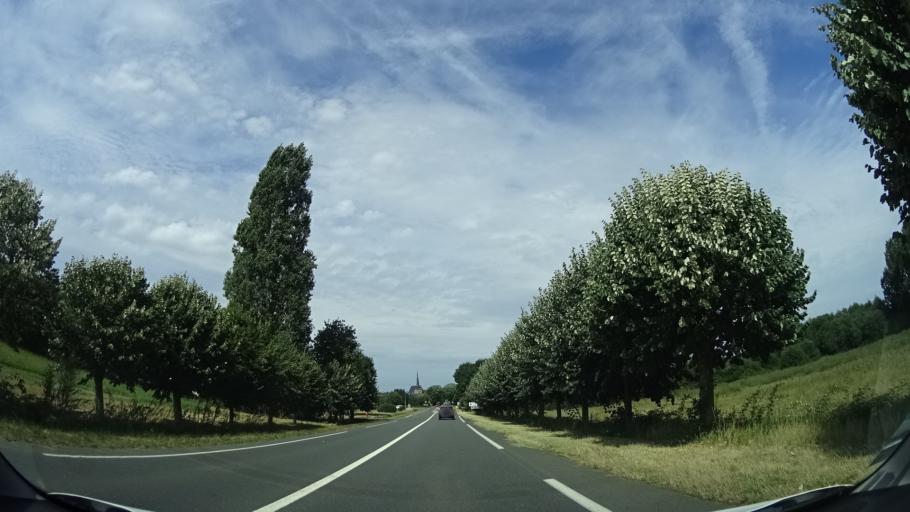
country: FR
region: Pays de la Loire
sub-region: Departement de la Sarthe
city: Bazouges-sur-le-Loir
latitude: 47.7444
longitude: -0.1449
